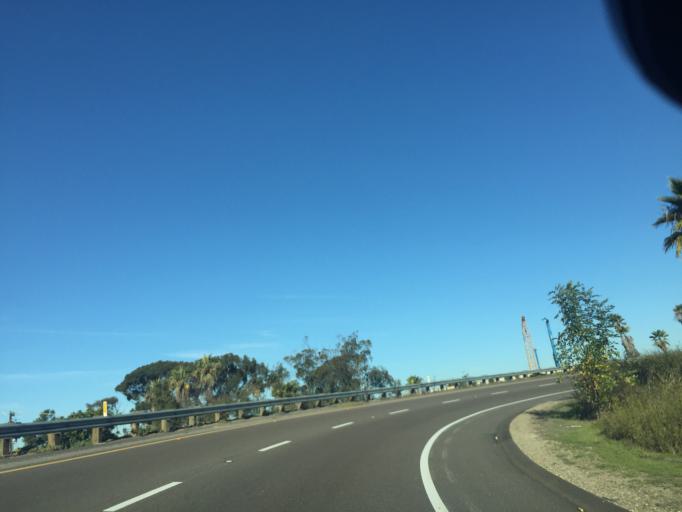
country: US
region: California
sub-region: San Diego County
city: San Diego
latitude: 32.7560
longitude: -117.2235
